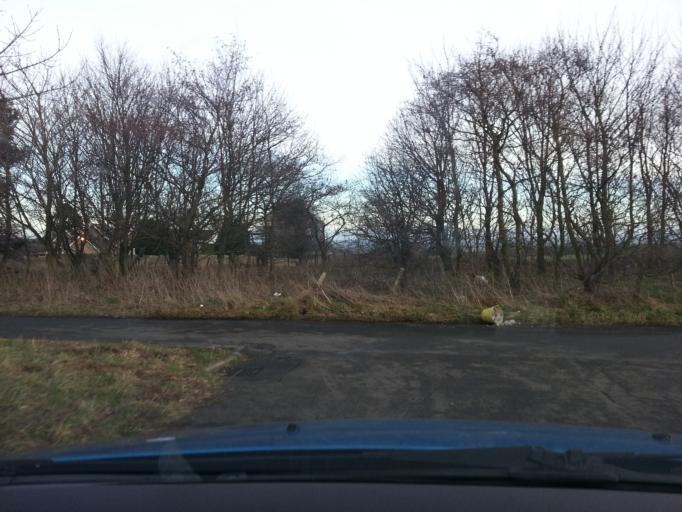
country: GB
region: England
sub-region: County Durham
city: Crook
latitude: 54.7372
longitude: -1.7410
